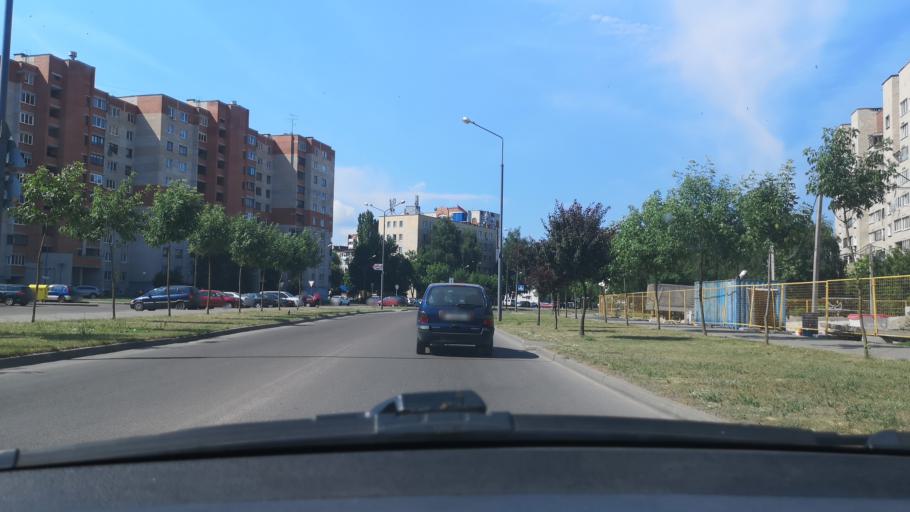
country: BY
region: Brest
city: Brest
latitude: 52.0954
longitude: 23.7042
